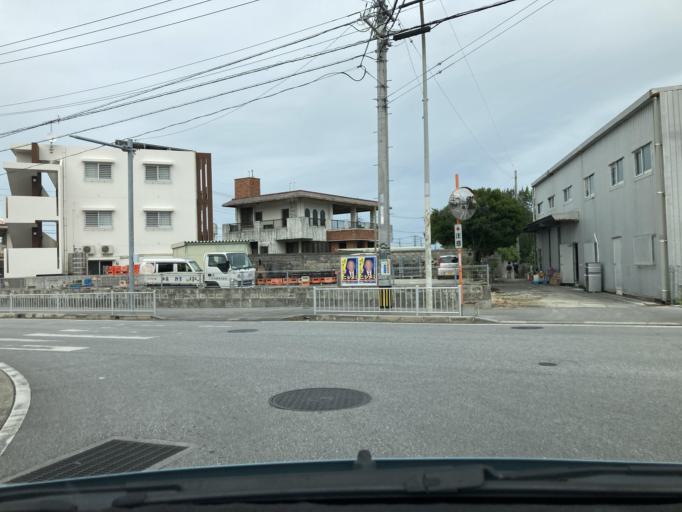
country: JP
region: Okinawa
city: Itoman
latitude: 26.1432
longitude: 127.6890
